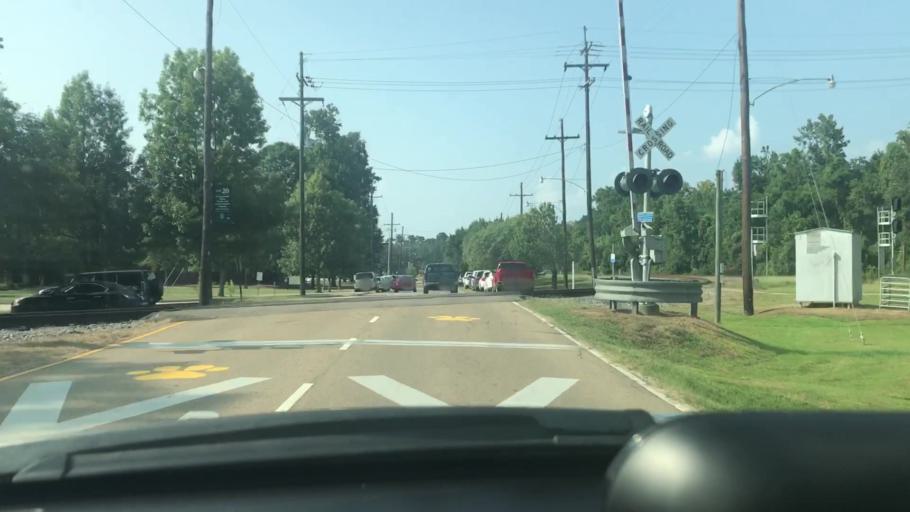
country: US
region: Louisiana
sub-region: Tangipahoa Parish
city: Hammond
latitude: 30.5083
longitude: -90.4627
